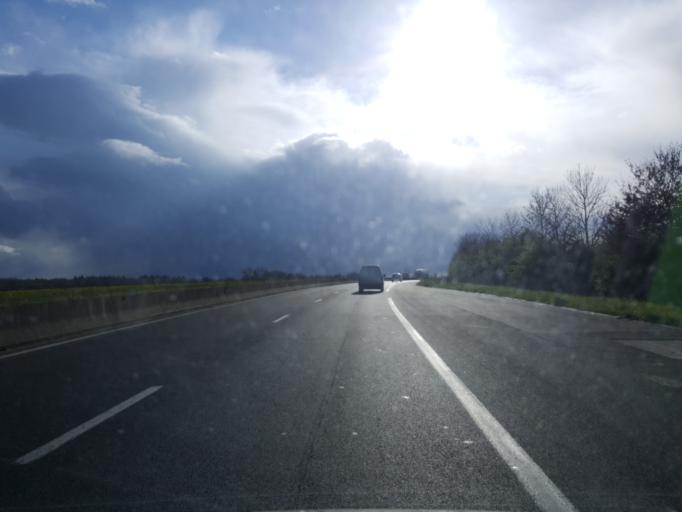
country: FR
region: Picardie
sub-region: Departement de l'Oise
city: Beauvais
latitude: 49.3861
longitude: 2.0677
